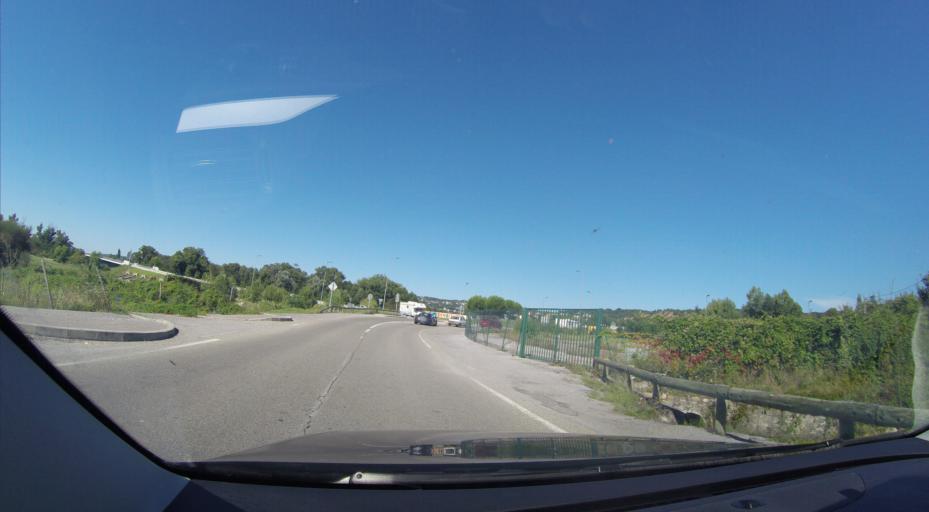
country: FR
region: Rhone-Alpes
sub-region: Departement de l'Ardeche
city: Saint-Privat
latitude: 44.6257
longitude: 4.4199
